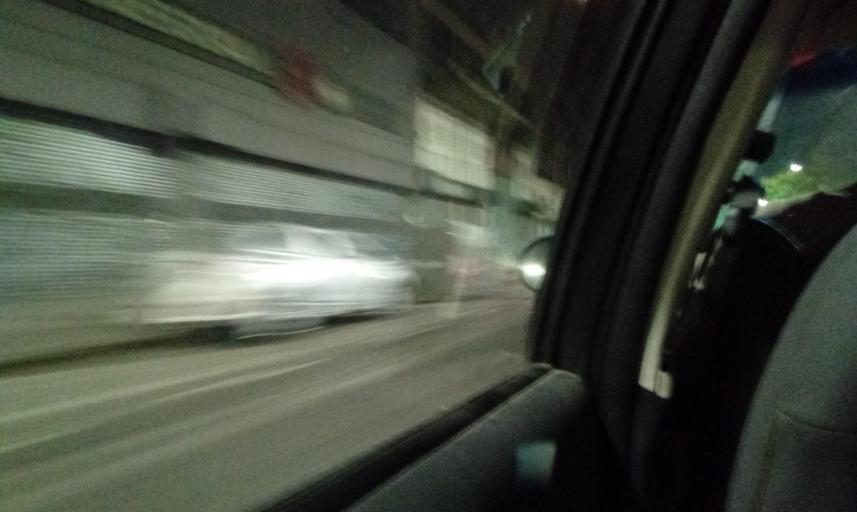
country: AR
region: Buenos Aires F.D.
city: Villa Santa Rita
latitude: -34.6287
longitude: -58.4807
